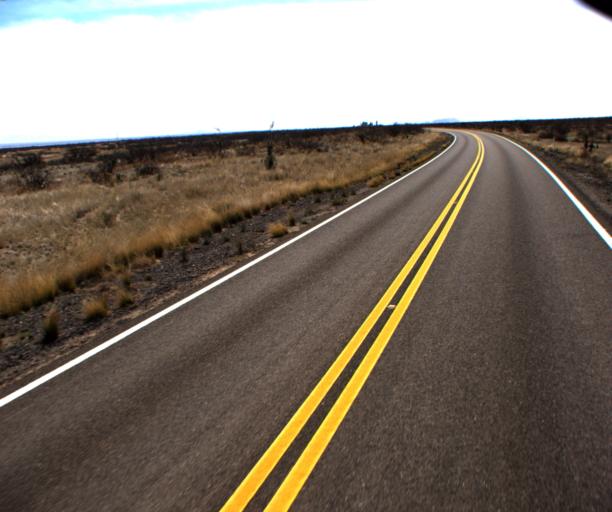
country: US
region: Arizona
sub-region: Cochise County
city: Willcox
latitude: 32.1444
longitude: -109.9328
